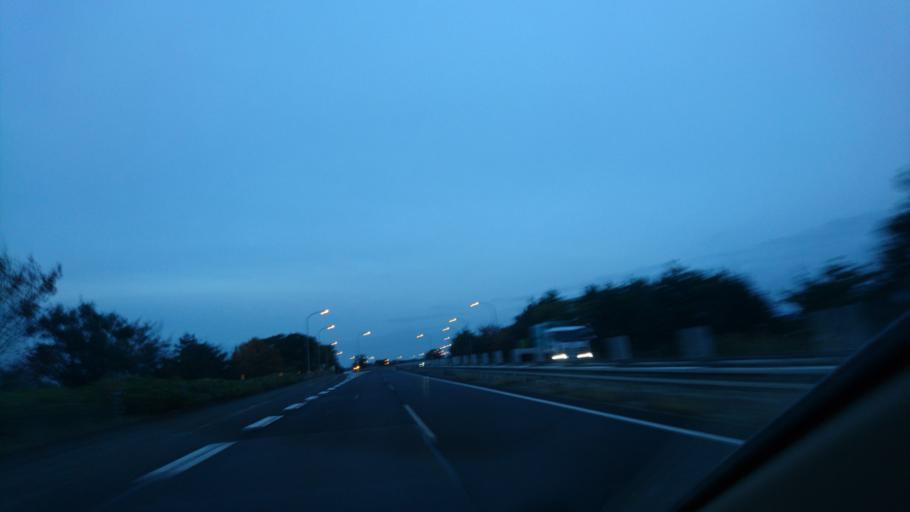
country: JP
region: Iwate
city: Morioka-shi
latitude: 39.6225
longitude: 141.1295
